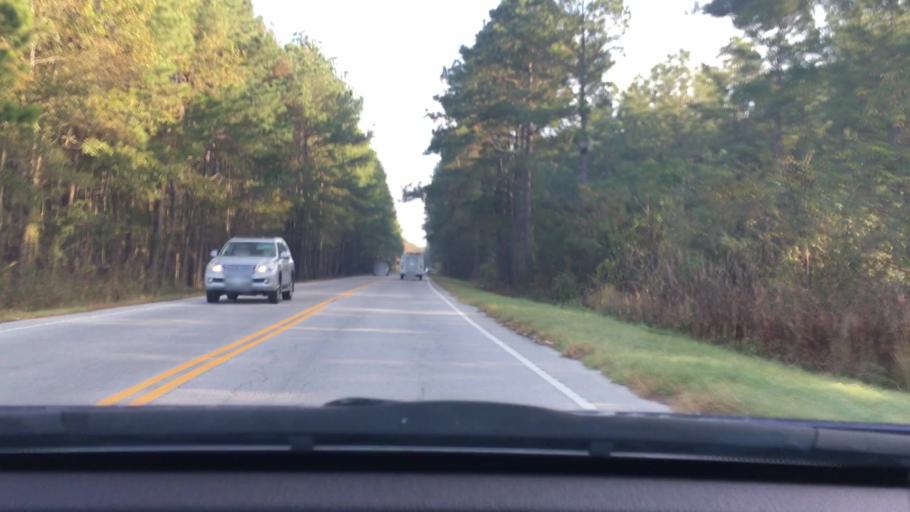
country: US
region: South Carolina
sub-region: Sumter County
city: East Sumter
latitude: 34.0314
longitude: -80.2722
